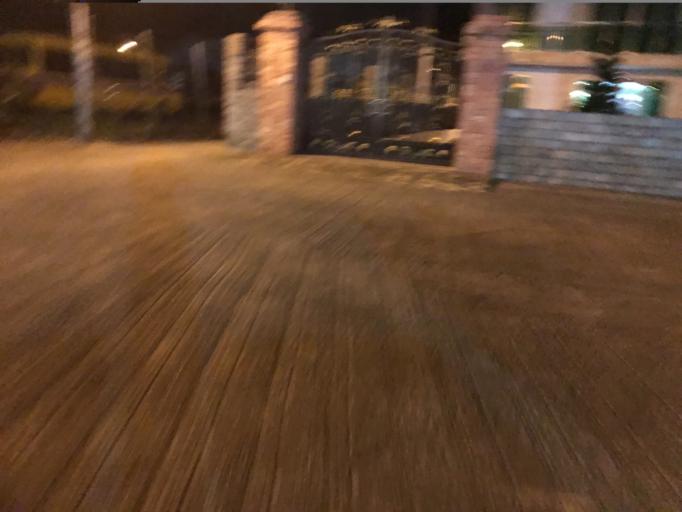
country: HK
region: Tai Po
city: Tai Po
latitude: 22.4684
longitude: 114.1504
